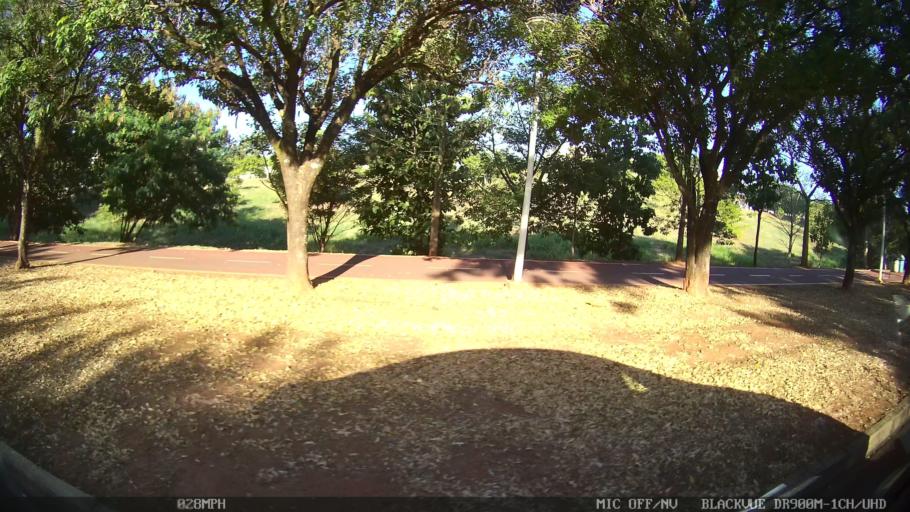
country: BR
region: Sao Paulo
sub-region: Sao Jose Do Rio Preto
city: Sao Jose do Rio Preto
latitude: -20.8400
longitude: -49.4104
